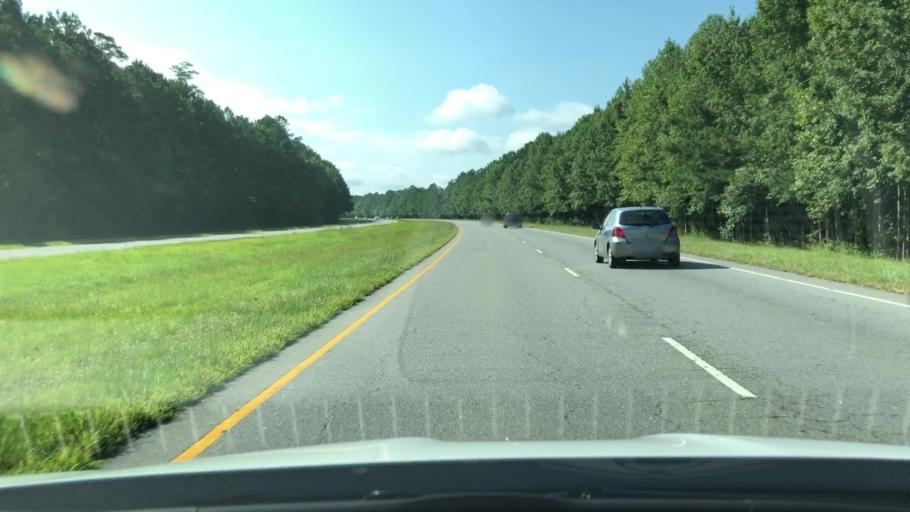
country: US
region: North Carolina
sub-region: Pasquotank County
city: Elizabeth City
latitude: 36.4091
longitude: -76.3393
